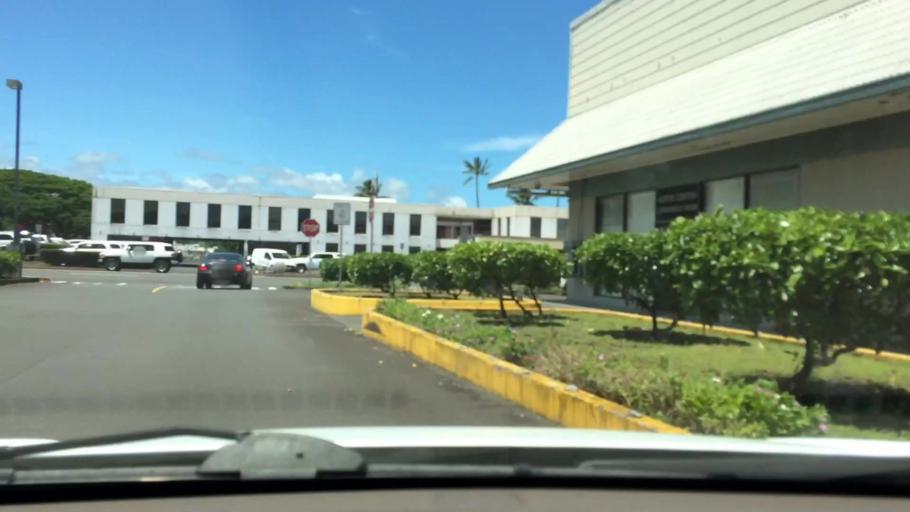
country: US
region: Hawaii
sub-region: Hawaii County
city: Hilo
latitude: 19.7190
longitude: -155.0793
